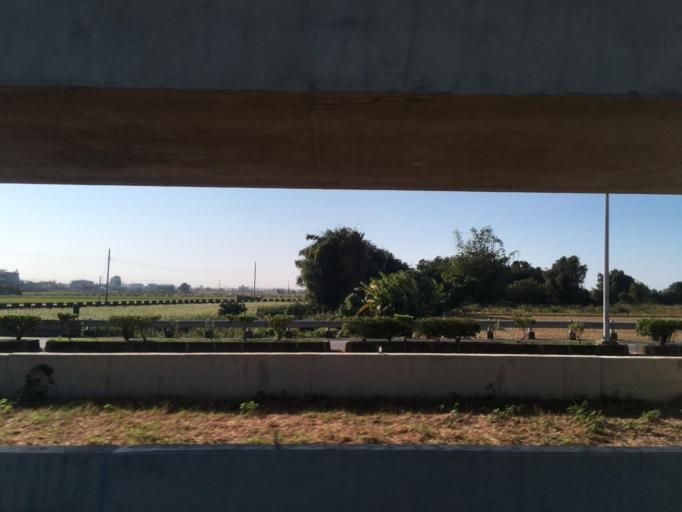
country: TW
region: Taiwan
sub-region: Chiayi
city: Taibao
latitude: 23.4356
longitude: 120.3229
